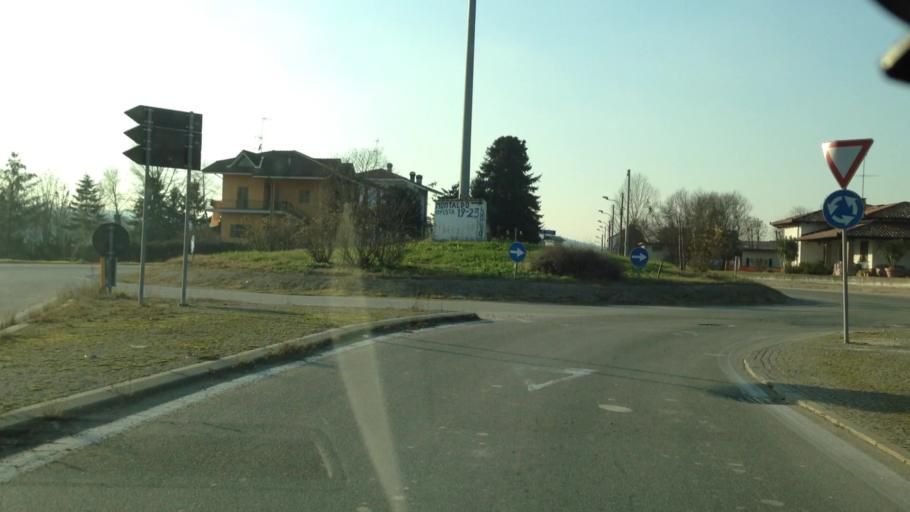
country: IT
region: Piedmont
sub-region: Provincia di Asti
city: Montaldo Scarampi
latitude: 44.8164
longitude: 8.2558
